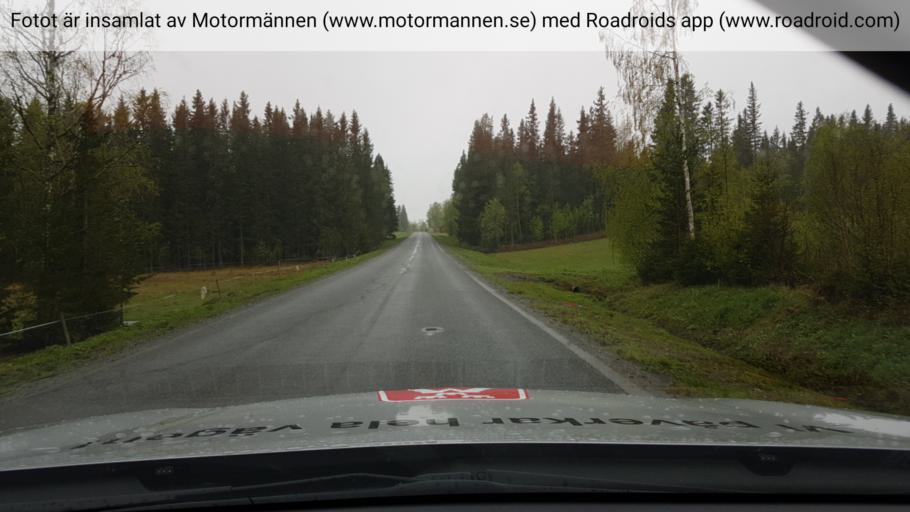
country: SE
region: Jaemtland
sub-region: Bergs Kommun
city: Hoverberg
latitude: 62.9827
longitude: 14.3249
